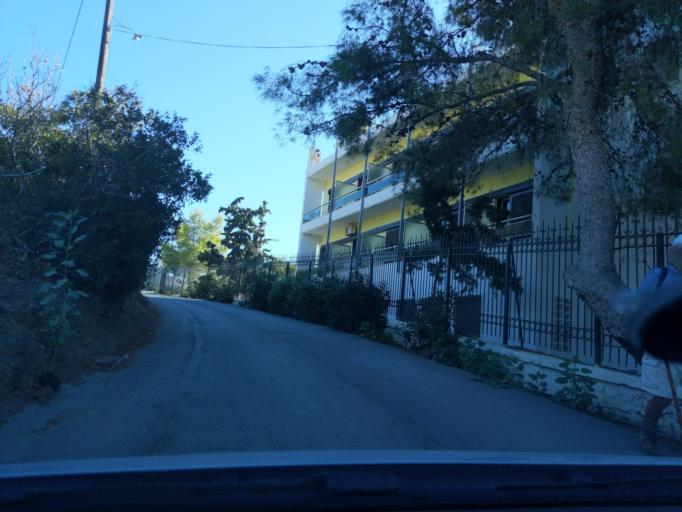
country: GR
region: Crete
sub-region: Nomos Irakleiou
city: Moires
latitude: 34.9325
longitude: 24.8032
